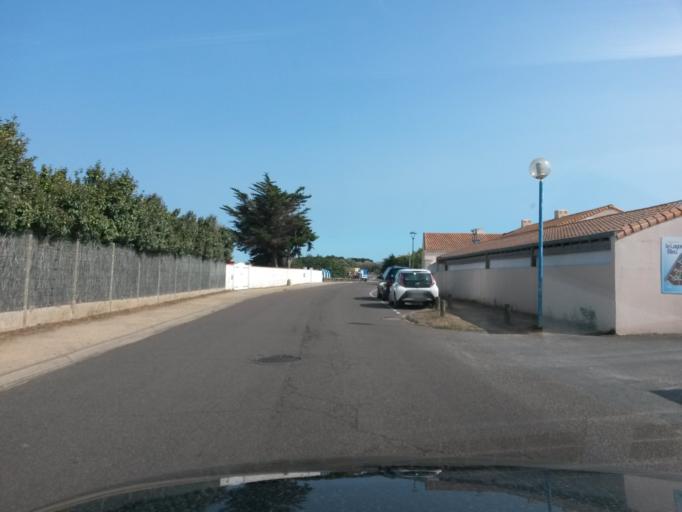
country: FR
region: Pays de la Loire
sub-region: Departement de la Vendee
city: Bretignolles-sur-Mer
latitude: 46.6170
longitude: -1.8609
